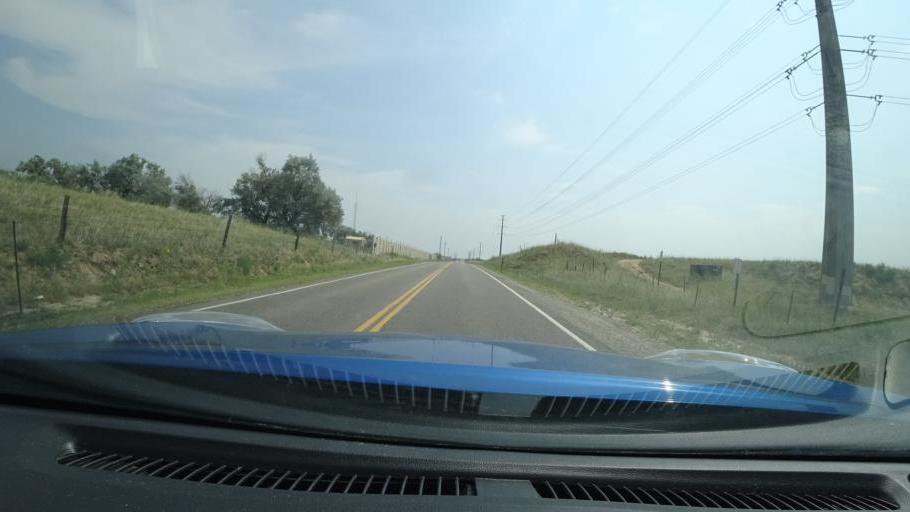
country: US
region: Colorado
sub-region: Adams County
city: Aurora
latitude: 39.7661
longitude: -104.7346
